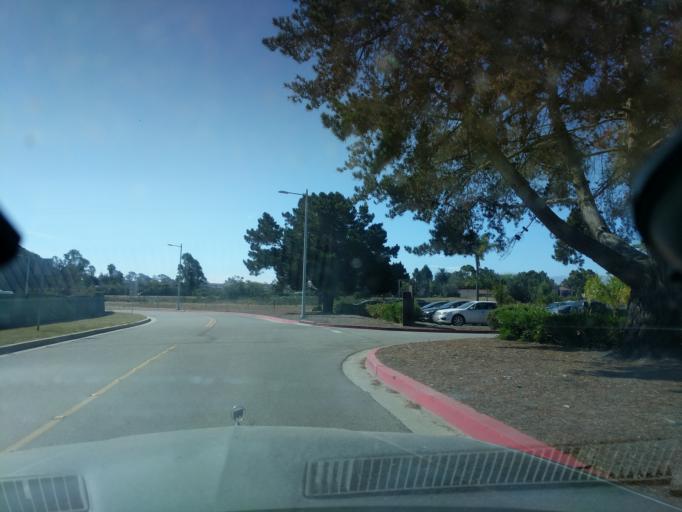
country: US
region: California
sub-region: Santa Barbara County
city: Isla Vista
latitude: 34.4225
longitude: -119.8616
